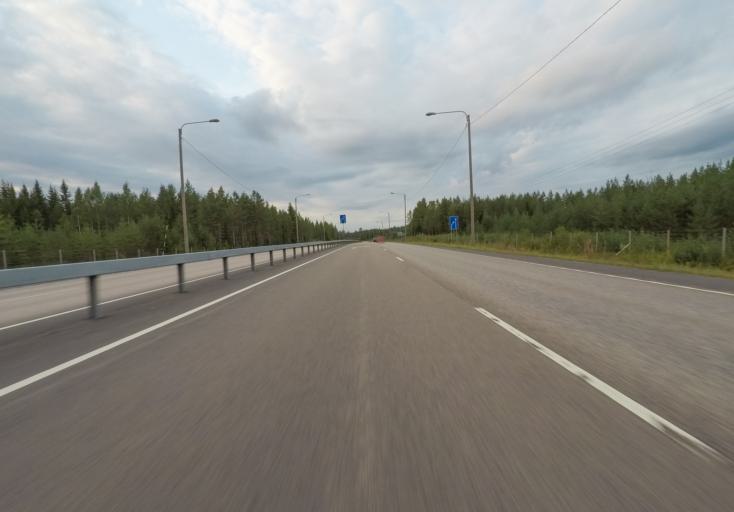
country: FI
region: Central Finland
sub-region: Joutsa
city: Joutsa
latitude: 61.8193
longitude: 26.0959
